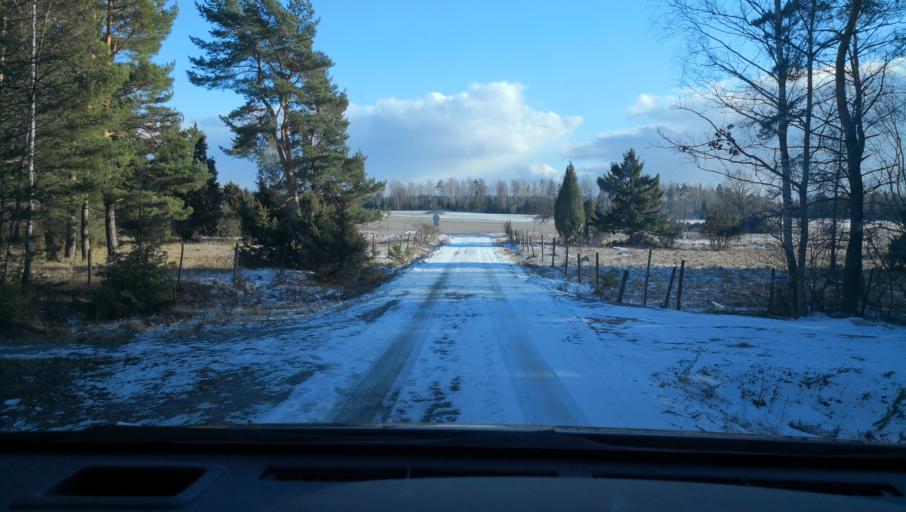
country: SE
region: Uppsala
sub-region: Enkopings Kommun
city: Hummelsta
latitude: 59.6241
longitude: 16.9319
